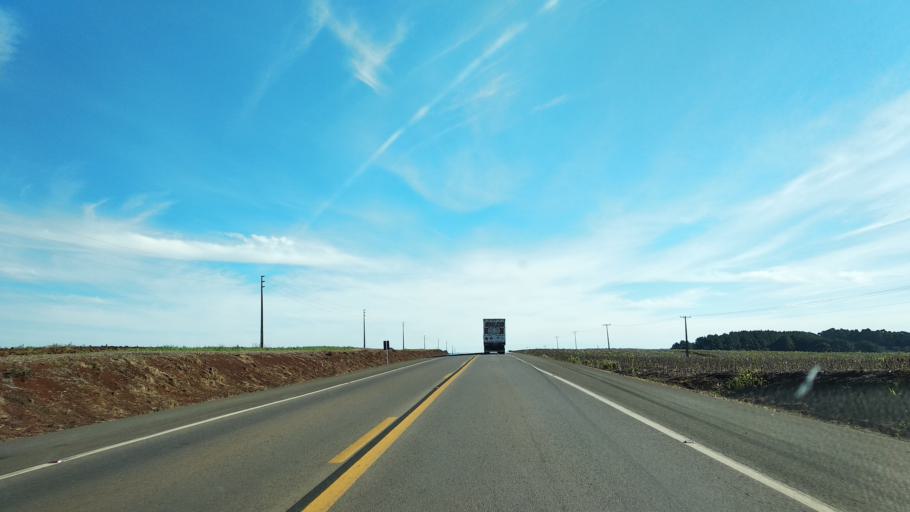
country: BR
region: Santa Catarina
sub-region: Campos Novos
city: Campos Novos
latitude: -27.4886
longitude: -51.3246
